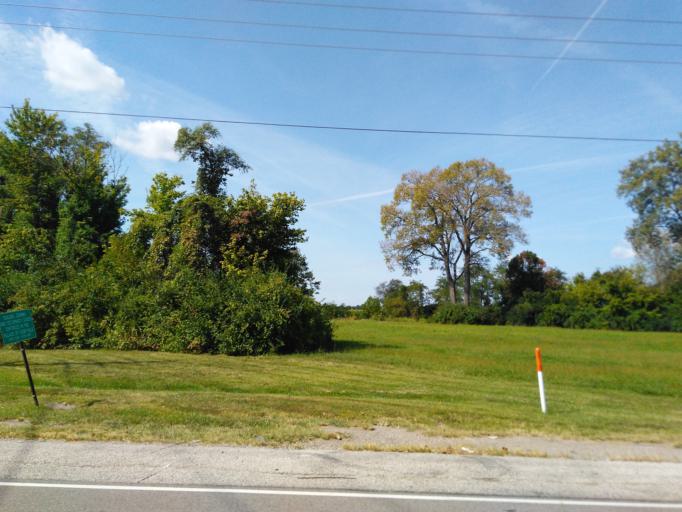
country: US
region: Illinois
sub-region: Saint Clair County
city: Caseyville
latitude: 38.6456
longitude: -90.0170
